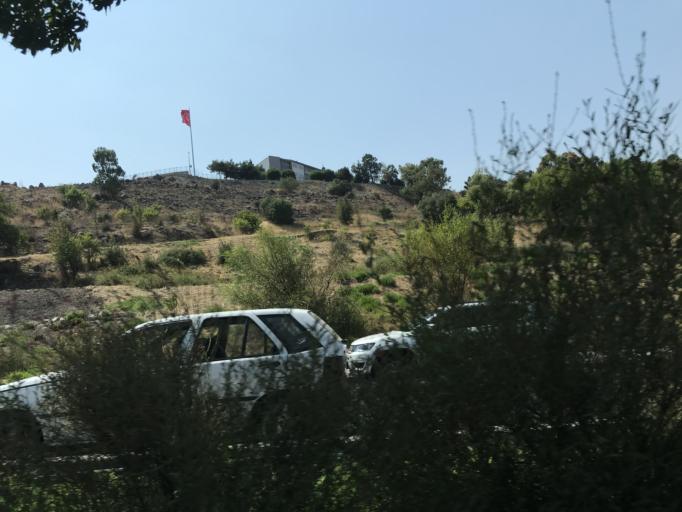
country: TR
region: Izmir
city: Izmir
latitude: 38.3965
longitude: 27.1382
